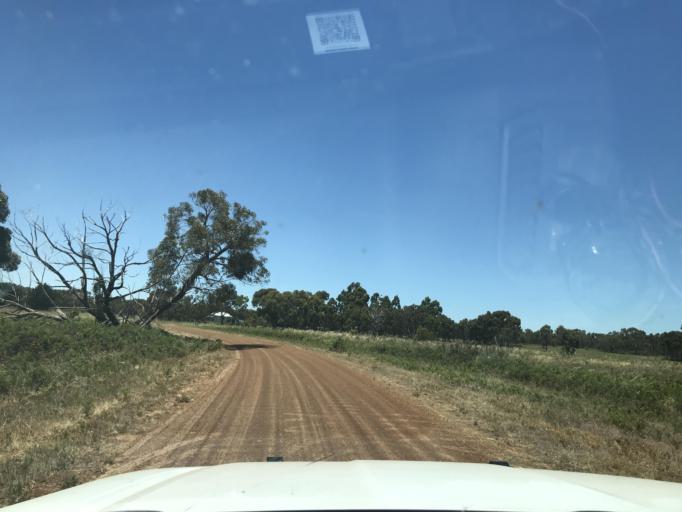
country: AU
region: South Australia
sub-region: Wattle Range
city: Penola
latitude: -37.0455
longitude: 141.3832
